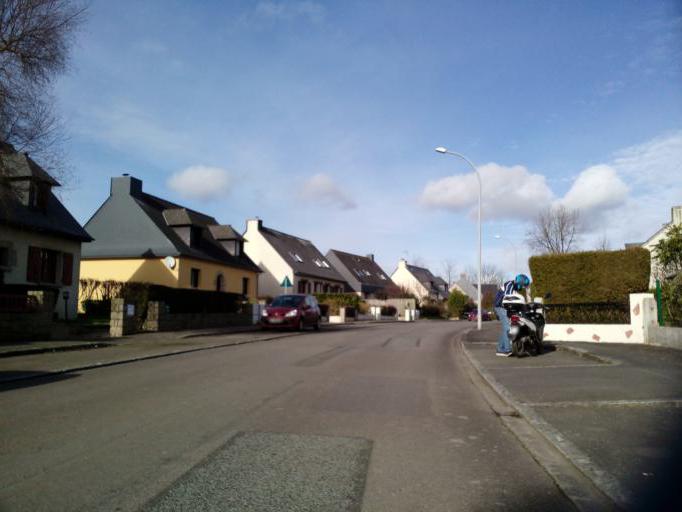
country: FR
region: Brittany
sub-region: Departement d'Ille-et-Vilaine
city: La Chapelle-des-Fougeretz
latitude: 48.1769
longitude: -1.7291
